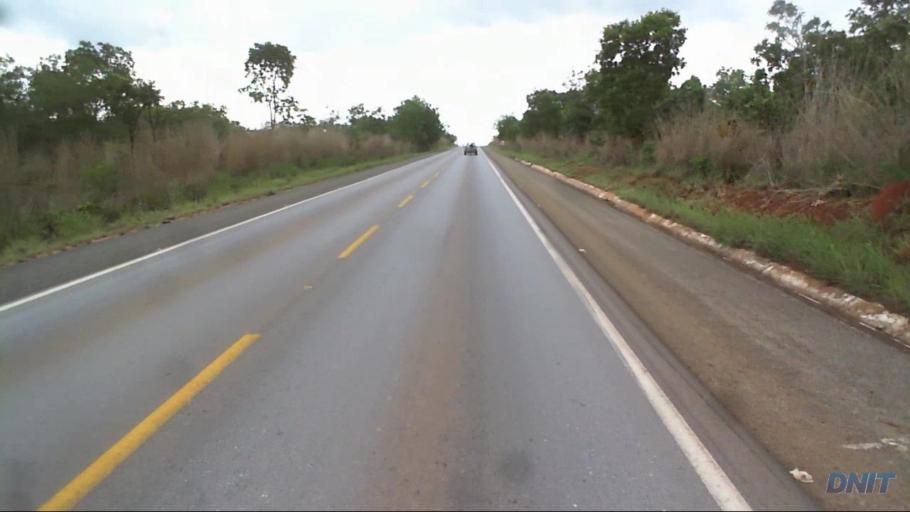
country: BR
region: Goias
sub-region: Uruacu
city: Uruacu
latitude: -14.7619
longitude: -49.0634
